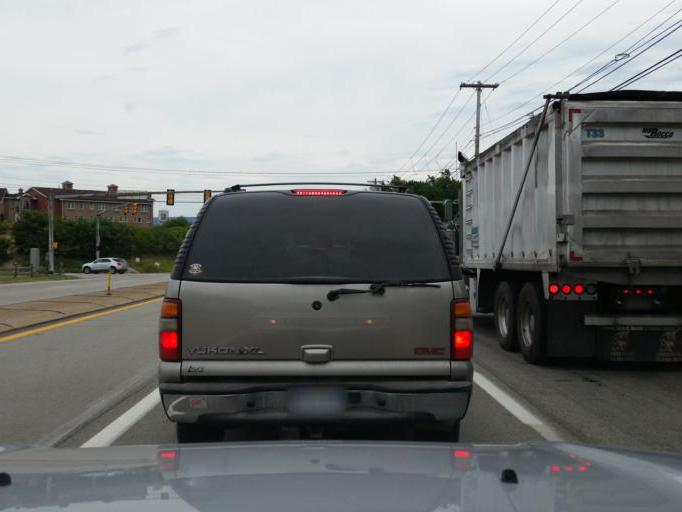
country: US
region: Pennsylvania
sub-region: Westmoreland County
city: Greensburg
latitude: 40.2907
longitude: -79.4649
